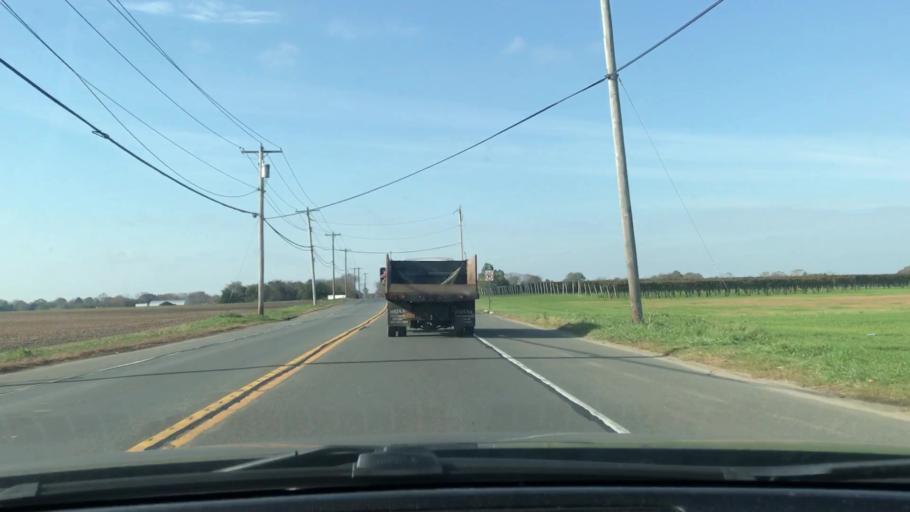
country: US
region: New York
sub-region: Suffolk County
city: Bridgehampton
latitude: 40.9436
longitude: -72.2694
